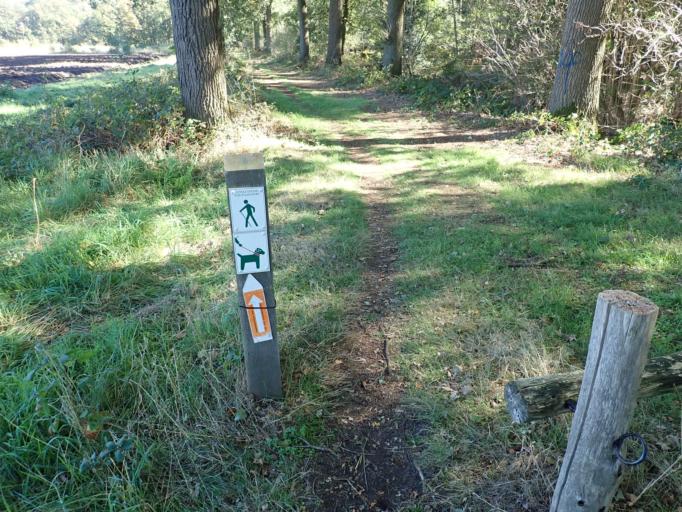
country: BE
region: Flanders
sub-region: Provincie Antwerpen
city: Merksplas
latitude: 51.4016
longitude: 4.8313
